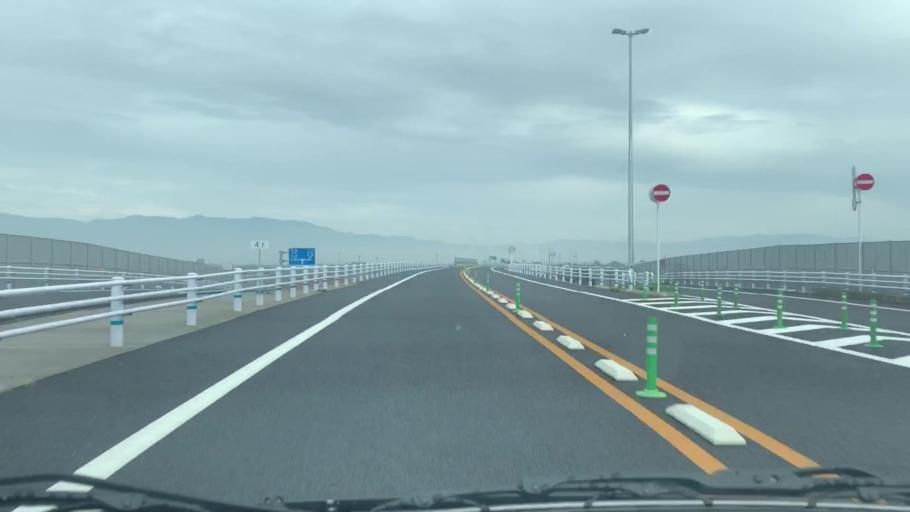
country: JP
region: Saga Prefecture
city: Saga-shi
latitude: 33.2190
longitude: 130.2144
